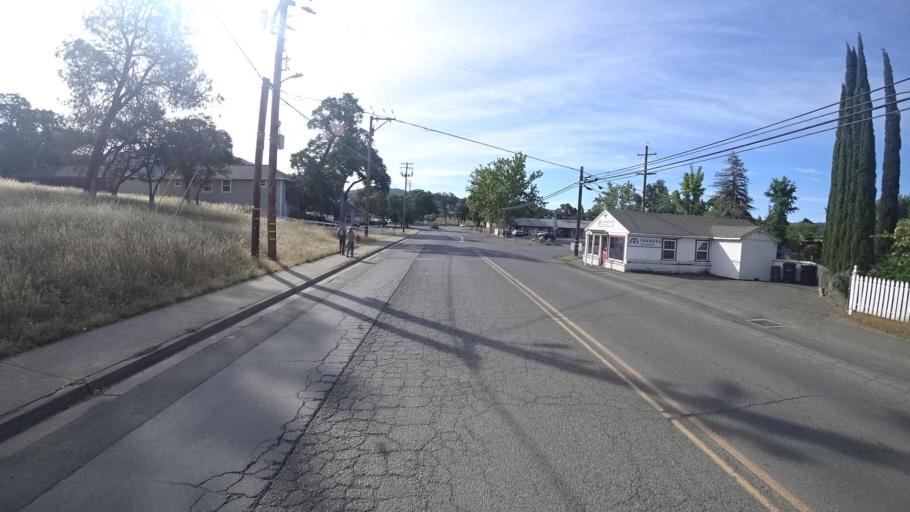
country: US
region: California
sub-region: Lake County
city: Kelseyville
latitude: 38.9762
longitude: -122.8331
